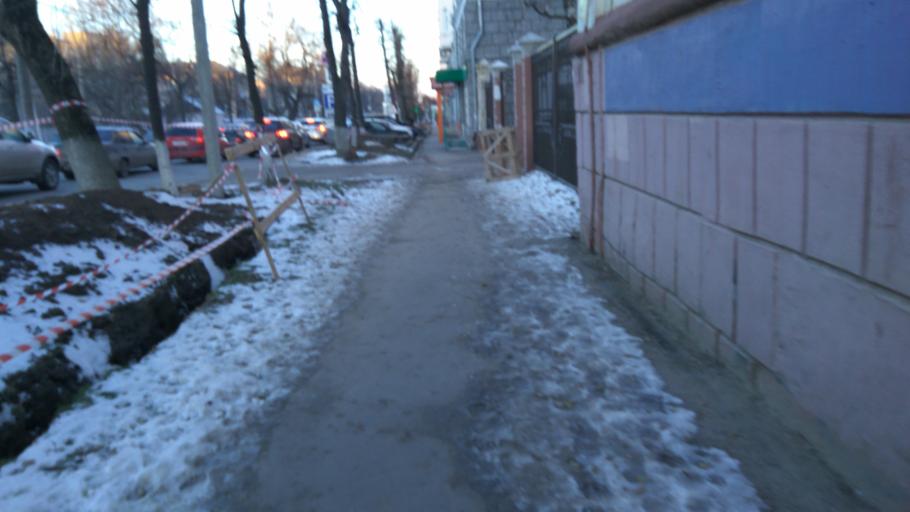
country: RU
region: Tula
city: Tula
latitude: 54.1810
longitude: 37.6004
